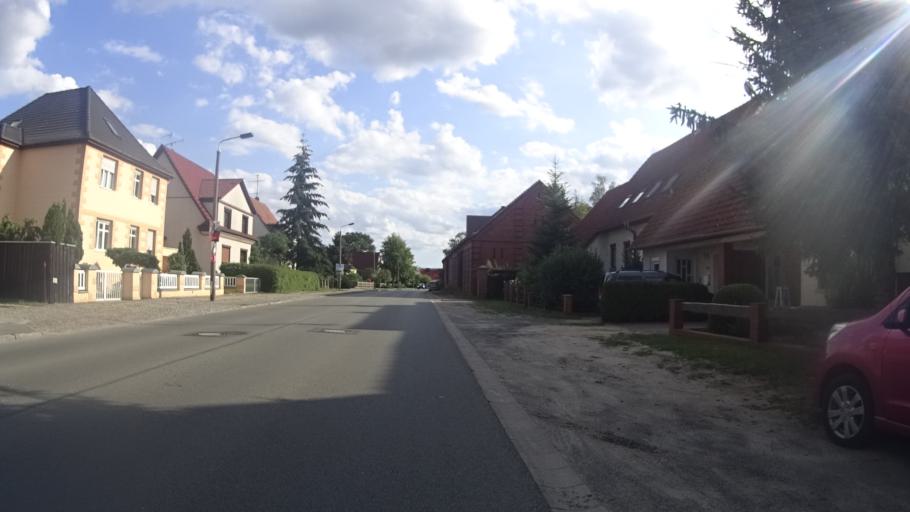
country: DE
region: Brandenburg
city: Rathenow
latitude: 52.6157
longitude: 12.3324
